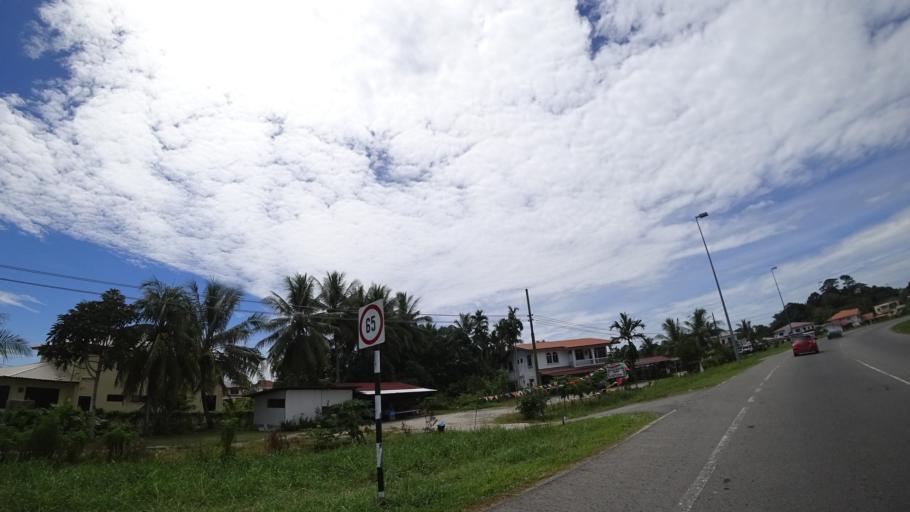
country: MY
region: Sarawak
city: Limbang
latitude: 4.8032
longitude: 114.8322
